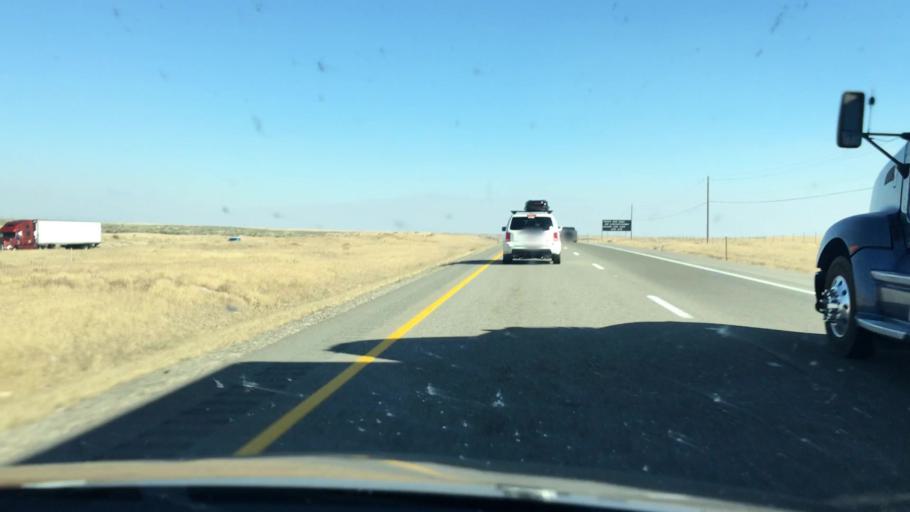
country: US
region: Idaho
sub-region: Ada County
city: Boise
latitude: 43.4524
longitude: -116.0808
